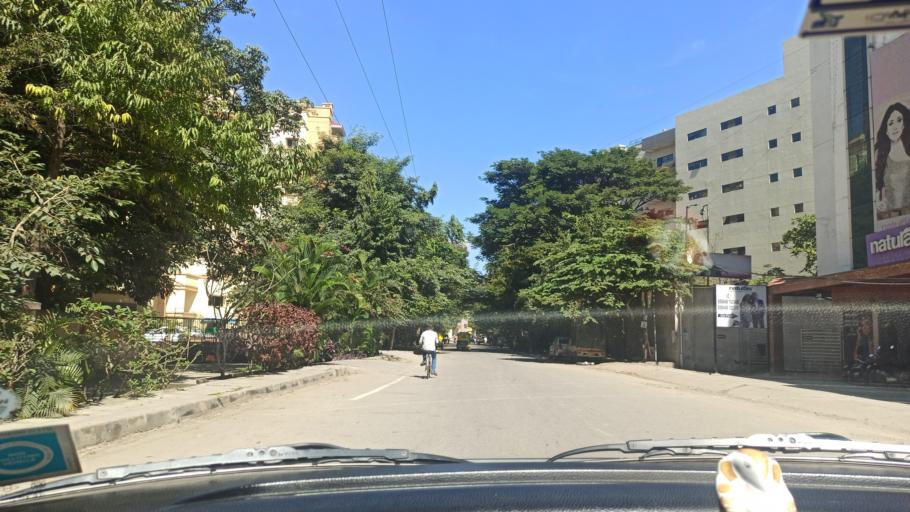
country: IN
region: Karnataka
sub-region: Bangalore Urban
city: Bangalore
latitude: 12.9232
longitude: 77.6695
